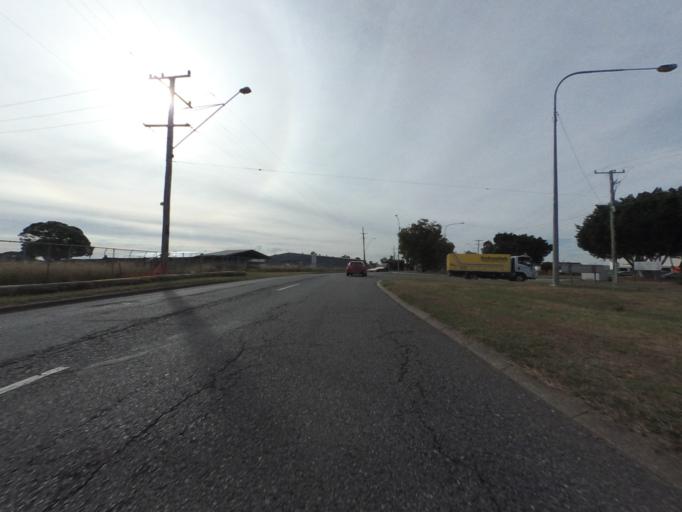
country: AU
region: Queensland
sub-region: Brisbane
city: Ascot
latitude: -27.4284
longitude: 153.0986
